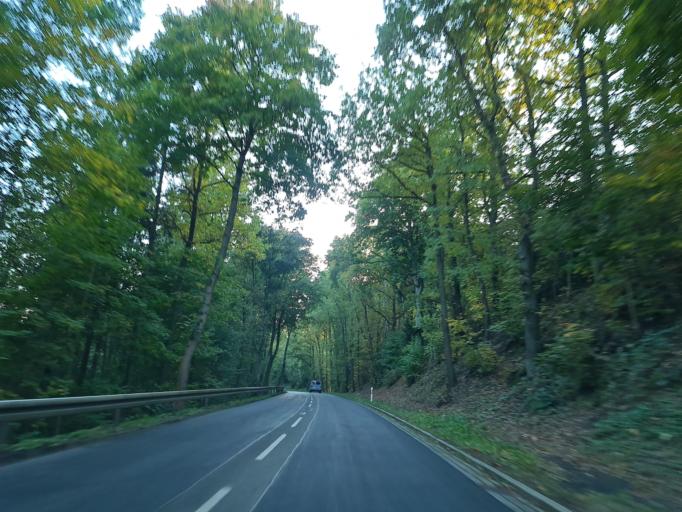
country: DE
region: Saxony
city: Elsterberg
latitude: 50.5800
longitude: 12.1306
